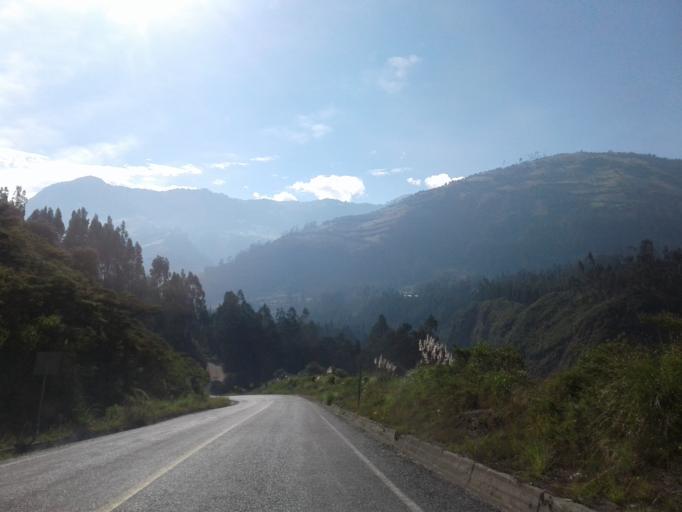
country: EC
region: Tungurahua
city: Banos
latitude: -1.5193
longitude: -78.5097
